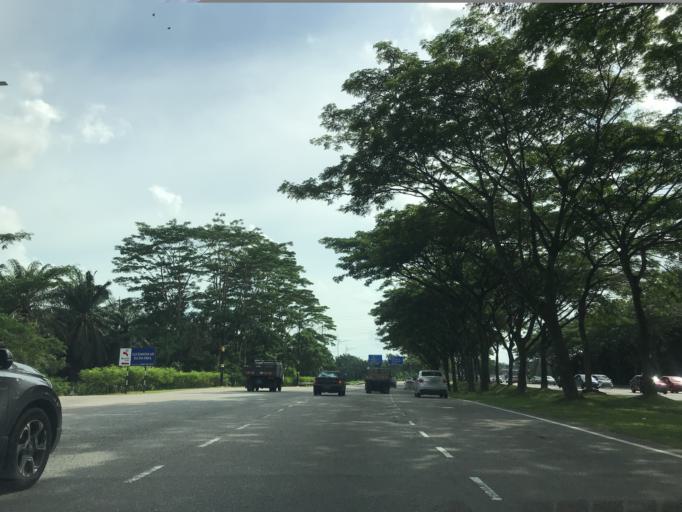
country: MY
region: Johor
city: Skudai
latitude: 1.5546
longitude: 103.6589
